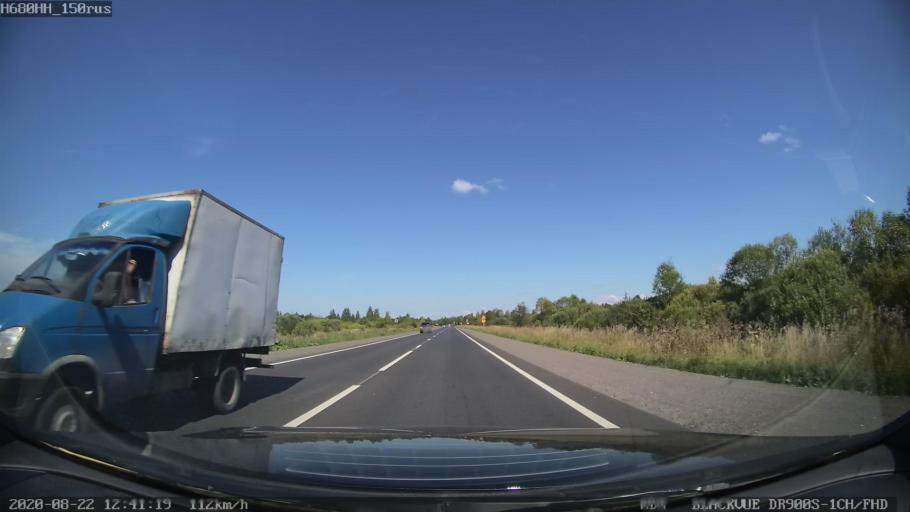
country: RU
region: Tverskaya
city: Rameshki
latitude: 57.3468
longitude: 36.0984
